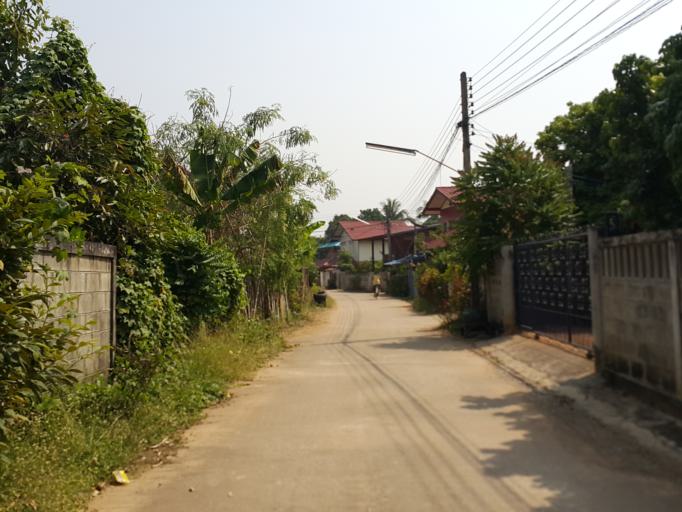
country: TH
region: Sukhothai
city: Thung Saliam
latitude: 17.3260
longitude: 99.5113
